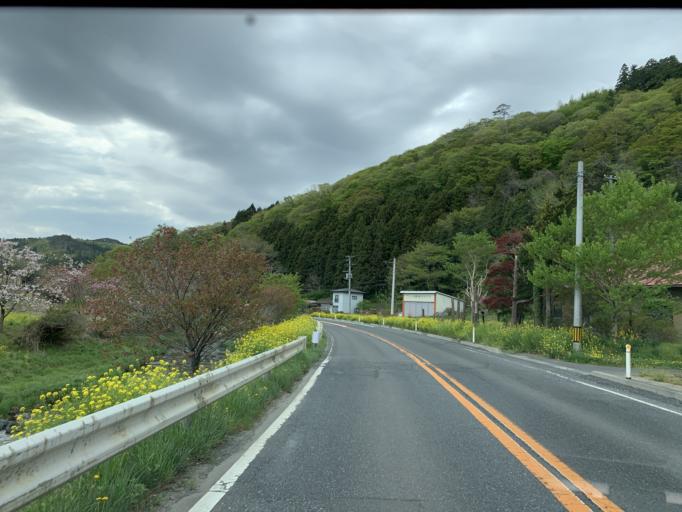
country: JP
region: Iwate
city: Ichinoseki
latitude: 38.7846
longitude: 141.3924
